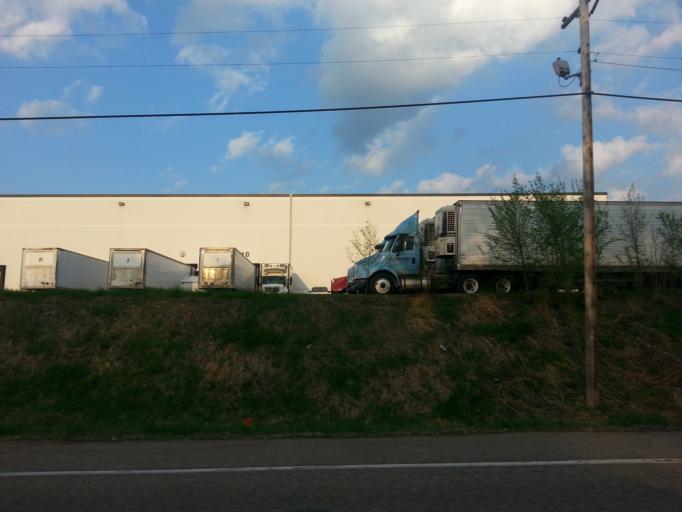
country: US
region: Minnesota
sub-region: Dakota County
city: Mendota Heights
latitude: 44.8696
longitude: -93.1725
